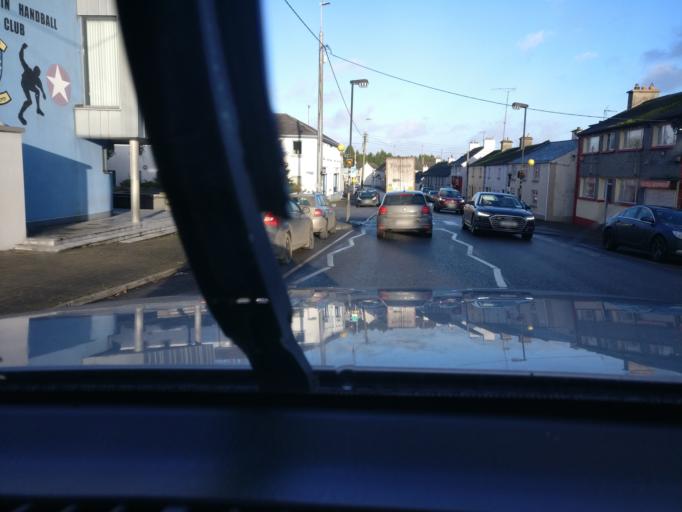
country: IE
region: Leinster
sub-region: An Iarmhi
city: Rathwire
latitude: 53.6120
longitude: -7.0927
